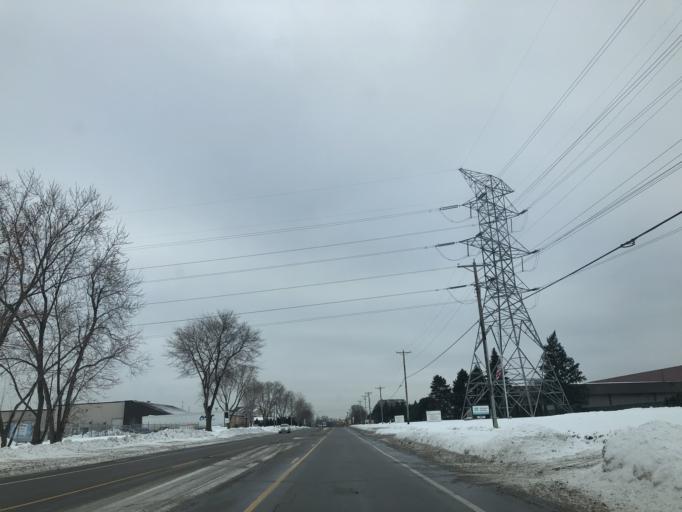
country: US
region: Minnesota
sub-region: Ramsey County
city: New Brighton
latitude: 45.0831
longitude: -93.1883
